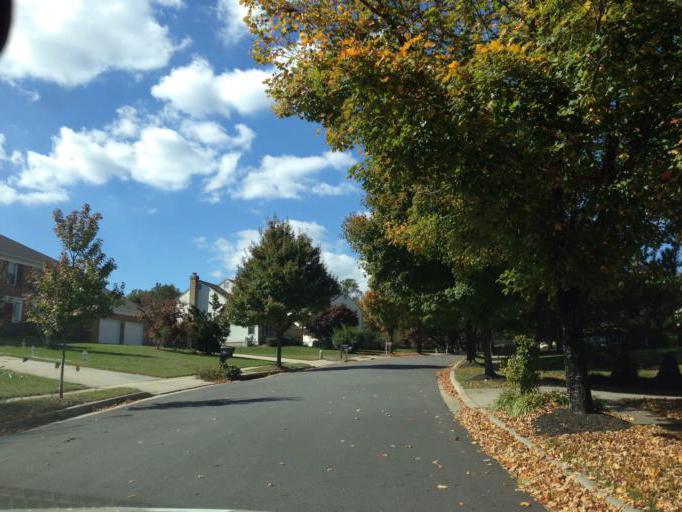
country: US
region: Maryland
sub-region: Howard County
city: North Laurel
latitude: 39.1376
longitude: -76.8981
